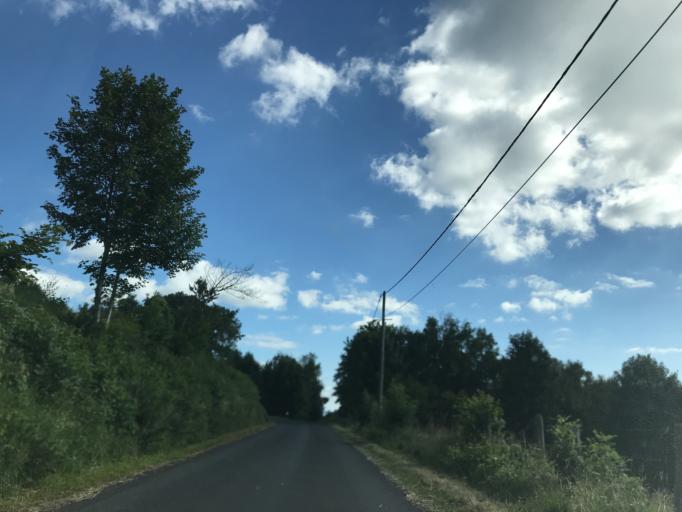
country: FR
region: Rhone-Alpes
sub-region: Departement de la Loire
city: Noiretable
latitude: 45.7524
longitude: 3.6990
